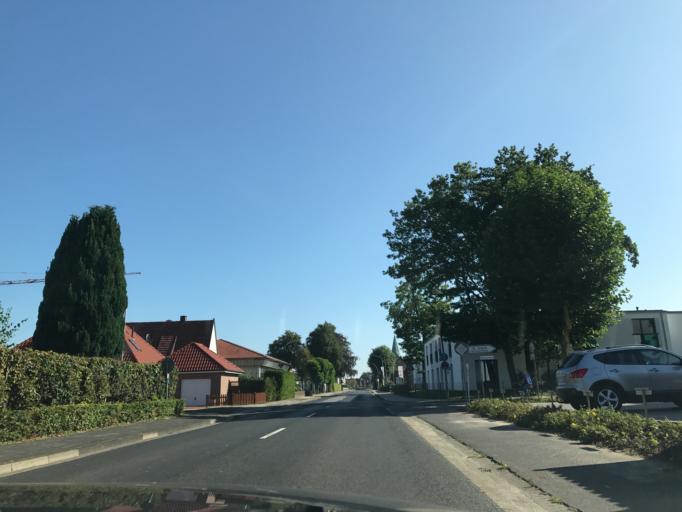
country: DE
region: Lower Saxony
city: Haselunne
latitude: 52.6699
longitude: 7.4772
